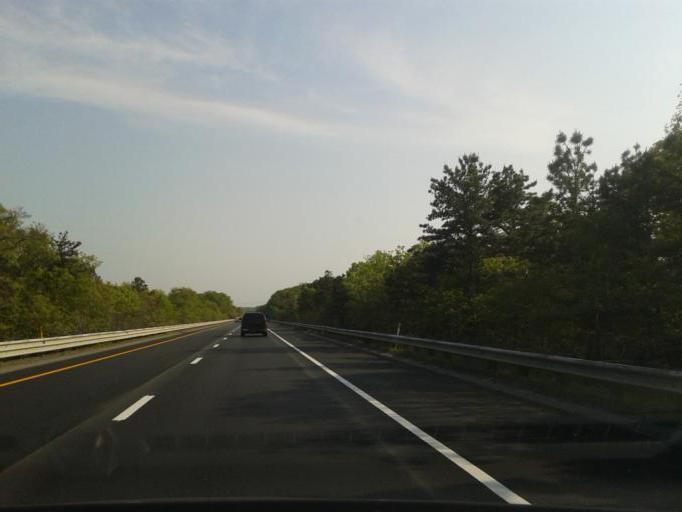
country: US
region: Massachusetts
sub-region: Barnstable County
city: North Falmouth
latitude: 41.6595
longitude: -70.6012
